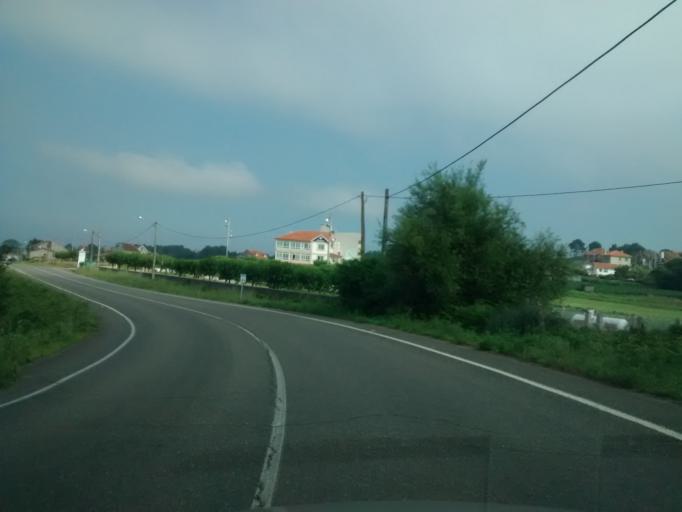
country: ES
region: Galicia
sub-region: Provincia de Pontevedra
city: Sanxenxo
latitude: 42.4081
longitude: -8.8542
